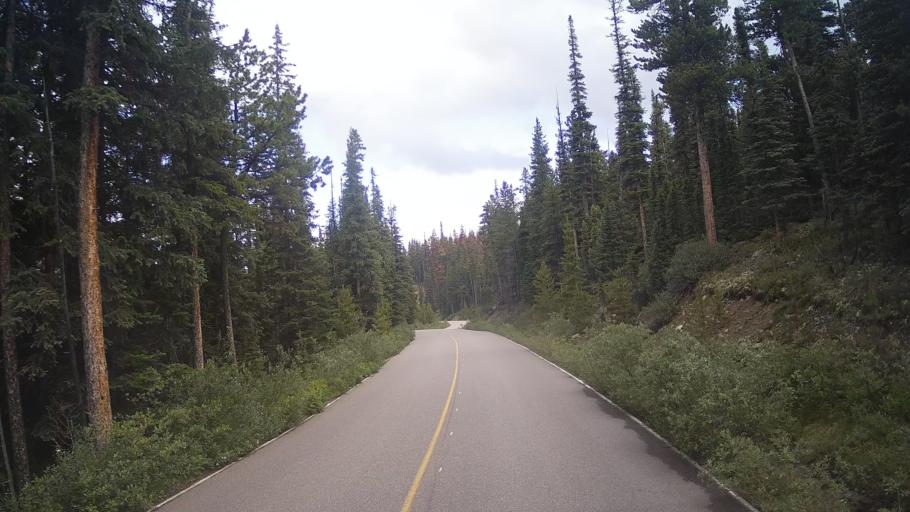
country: CA
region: Alberta
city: Jasper Park Lodge
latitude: 52.7120
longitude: -118.0557
